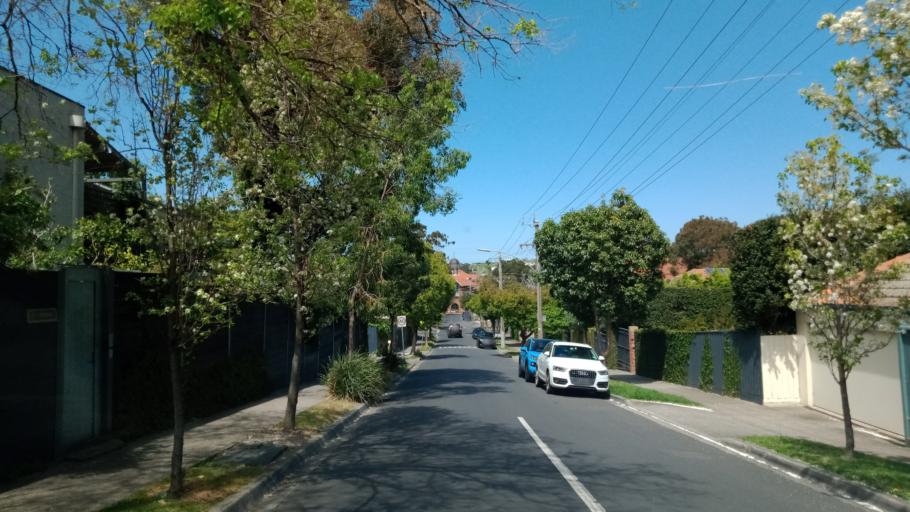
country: AU
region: Victoria
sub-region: Boroondara
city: Hawthorn East
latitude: -37.8321
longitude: 145.0305
